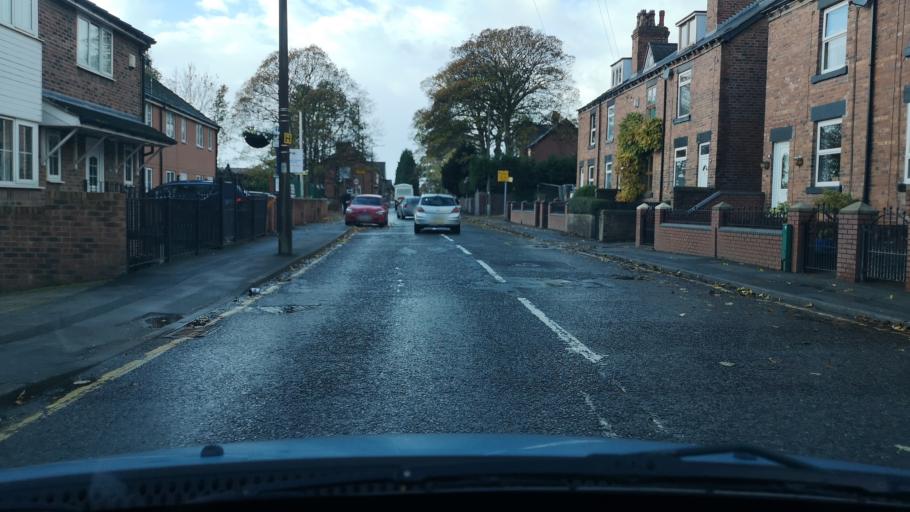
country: GB
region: England
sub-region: Barnsley
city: Royston
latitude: 53.5993
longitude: -1.4524
